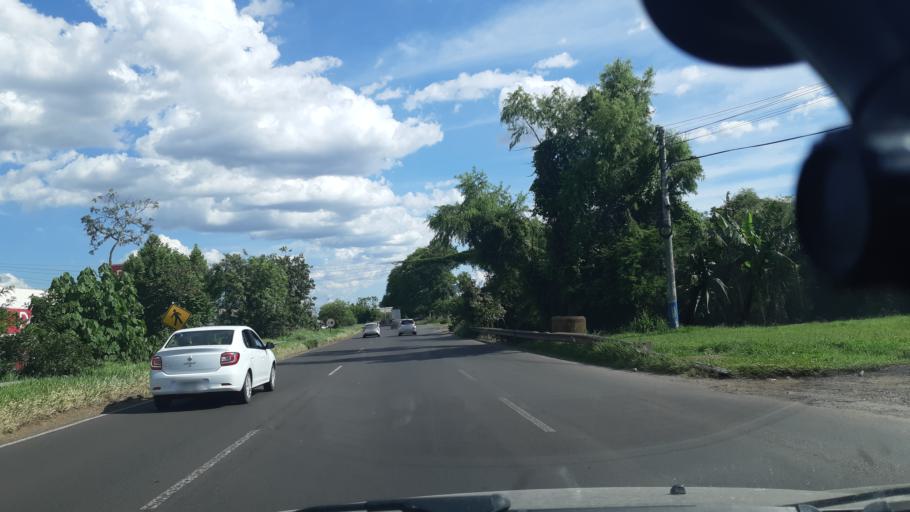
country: BR
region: Rio Grande do Sul
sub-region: Novo Hamburgo
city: Novo Hamburgo
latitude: -29.6580
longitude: -51.1443
